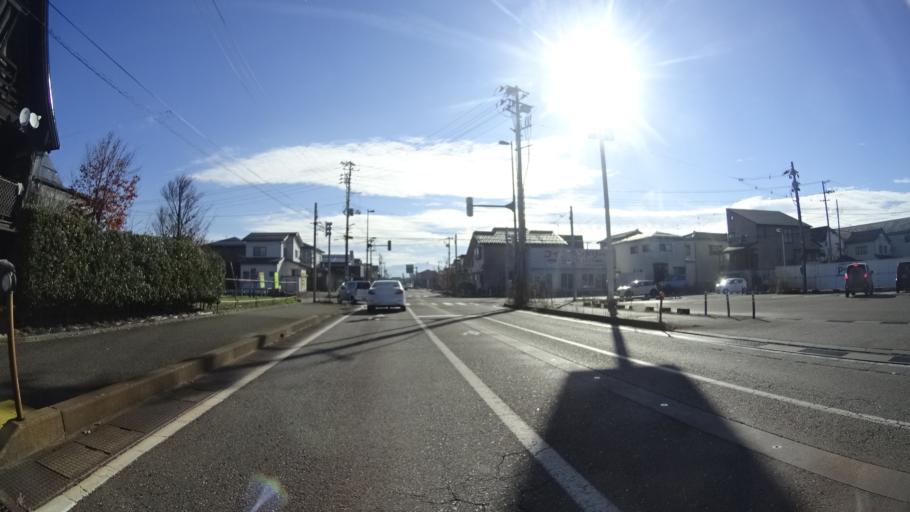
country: JP
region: Niigata
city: Mitsuke
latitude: 37.5441
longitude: 138.8853
